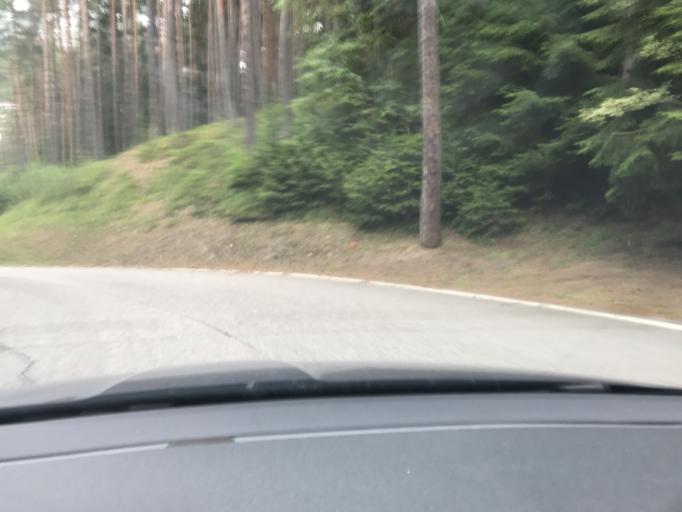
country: IT
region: Trentino-Alto Adige
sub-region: Bolzano
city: Bressanone
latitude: 46.6845
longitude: 11.6770
